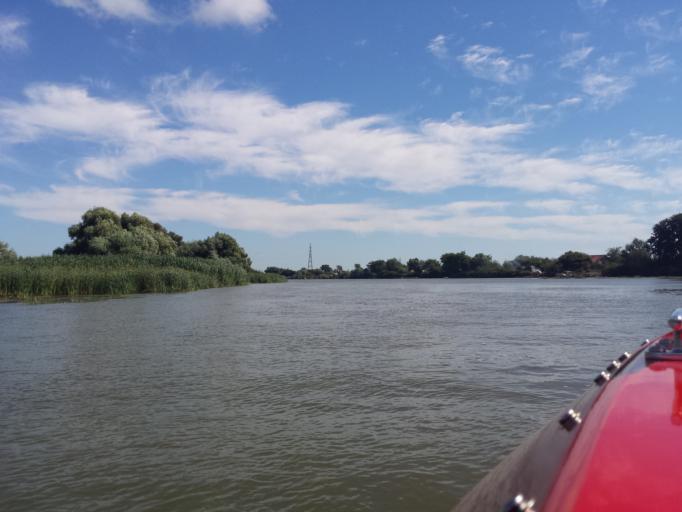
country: RO
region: Tulcea
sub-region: Comuna Crisan
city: Crisan
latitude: 45.2183
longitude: 29.2307
